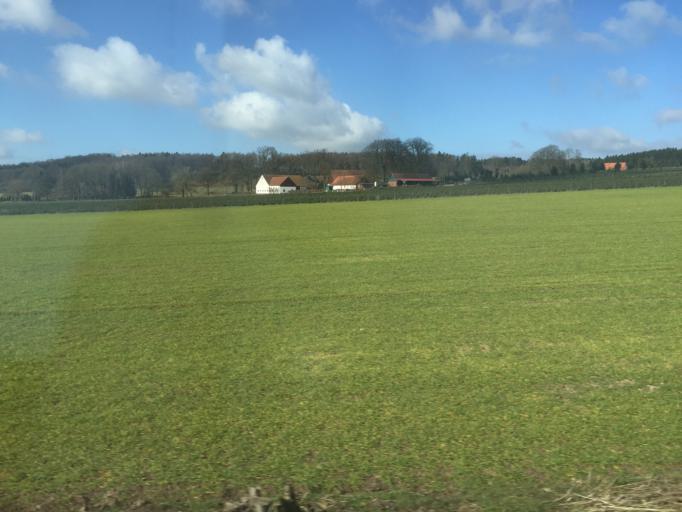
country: DE
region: Lower Saxony
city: Belm
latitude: 52.3212
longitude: 8.1419
